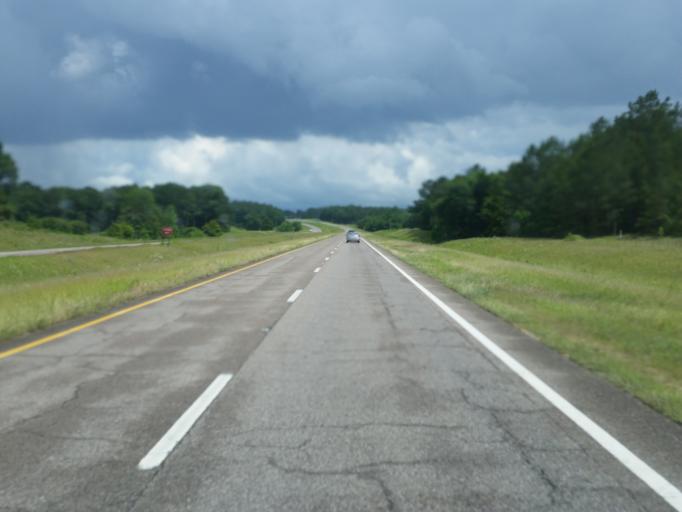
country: US
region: Mississippi
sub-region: George County
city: Lucedale
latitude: 30.9341
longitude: -88.5234
